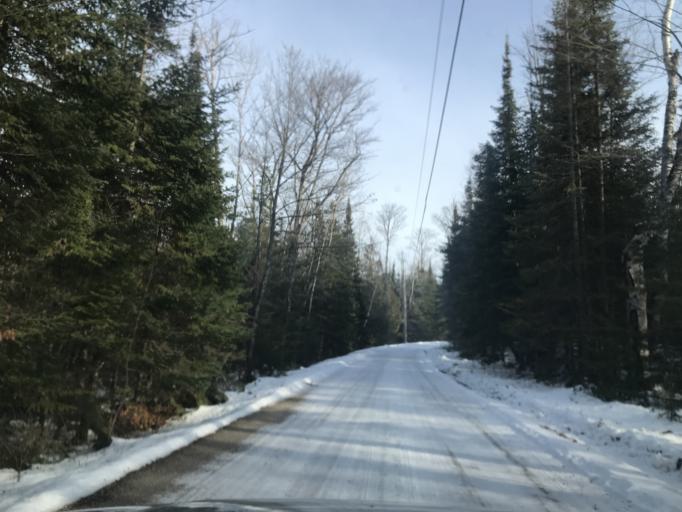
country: US
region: Wisconsin
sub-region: Door County
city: Sturgeon Bay
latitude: 45.1549
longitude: -87.0484
